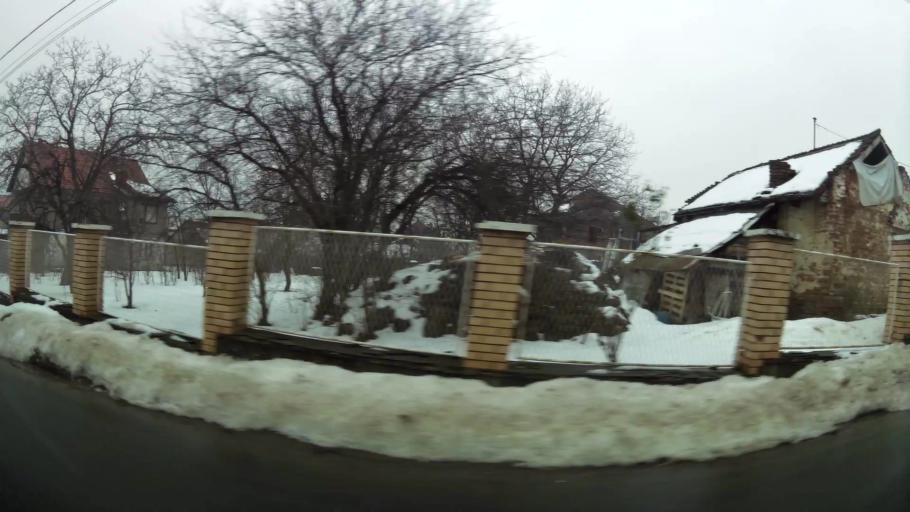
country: RS
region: Central Serbia
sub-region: Belgrade
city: Zvezdara
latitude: 44.7608
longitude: 20.5181
